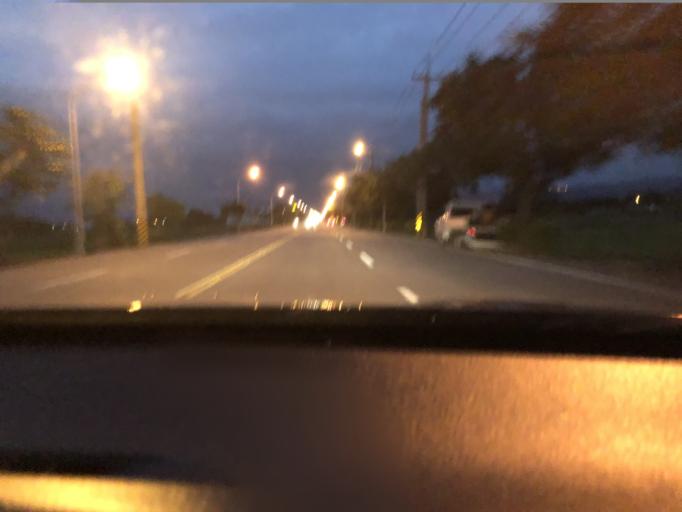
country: TW
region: Taiwan
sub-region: Hualien
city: Hualian
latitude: 23.9493
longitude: 121.5647
